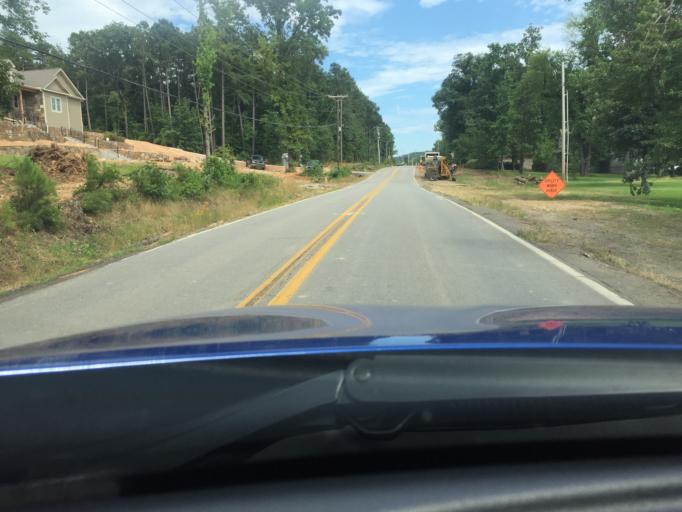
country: US
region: Arkansas
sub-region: Pulaski County
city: Maumelle
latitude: 34.8078
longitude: -92.4397
